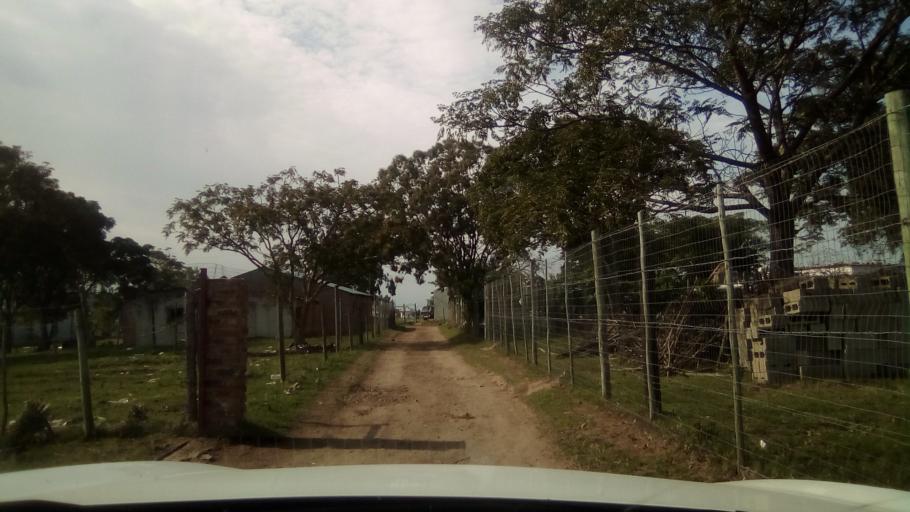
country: ZA
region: Eastern Cape
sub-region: Buffalo City Metropolitan Municipality
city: Bhisho
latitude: -32.9870
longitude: 27.2716
